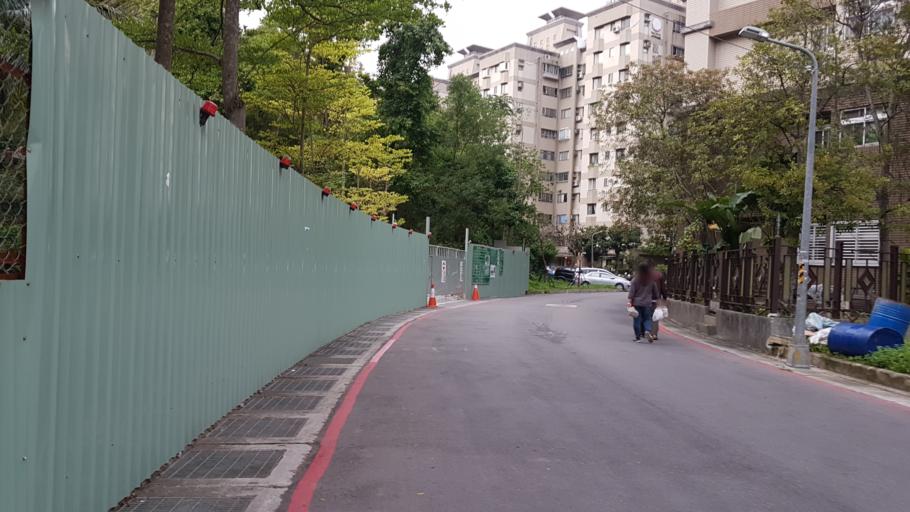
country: TW
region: Taipei
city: Taipei
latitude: 25.0039
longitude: 121.5484
